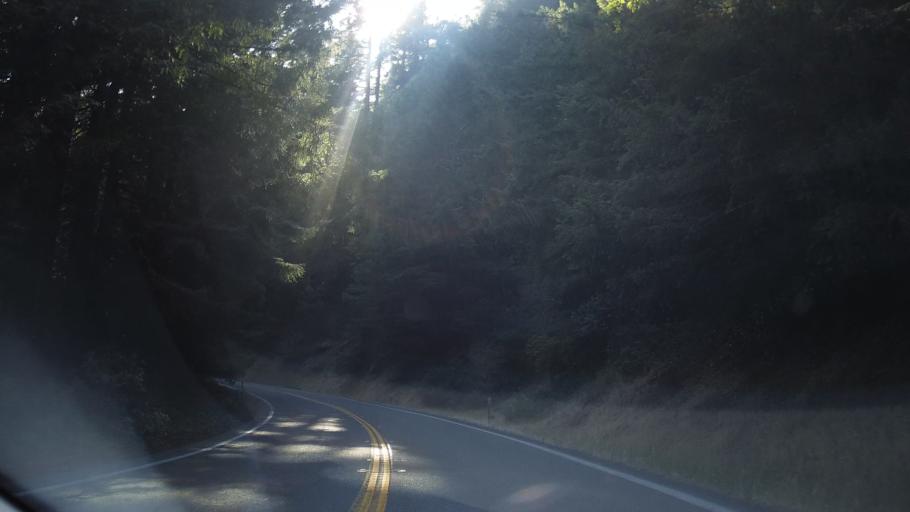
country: US
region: California
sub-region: Mendocino County
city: Brooktrails
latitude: 39.3486
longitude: -123.5153
